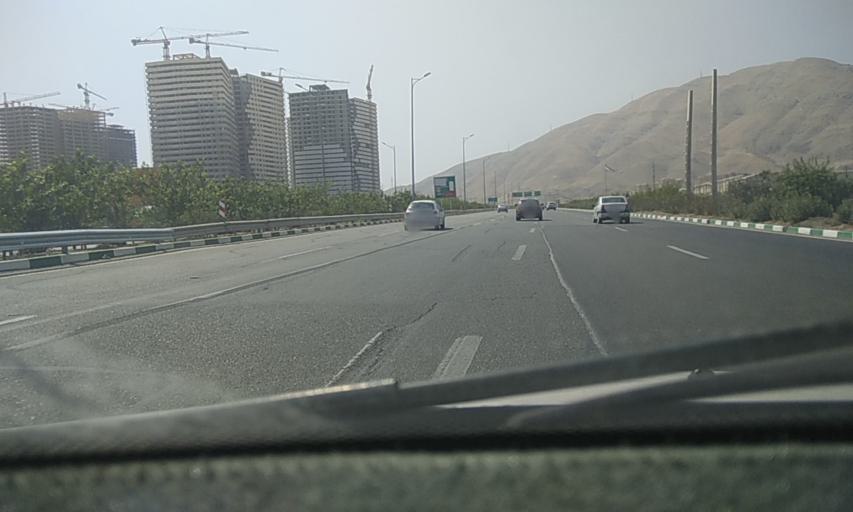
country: IR
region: Tehran
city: Shahr-e Qods
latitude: 35.7563
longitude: 51.1859
